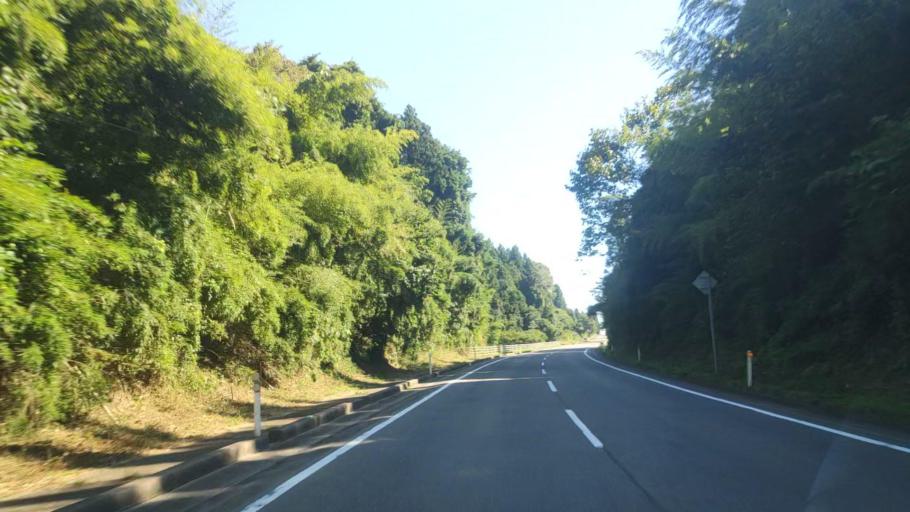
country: JP
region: Ishikawa
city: Nanao
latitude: 37.3757
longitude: 137.2342
